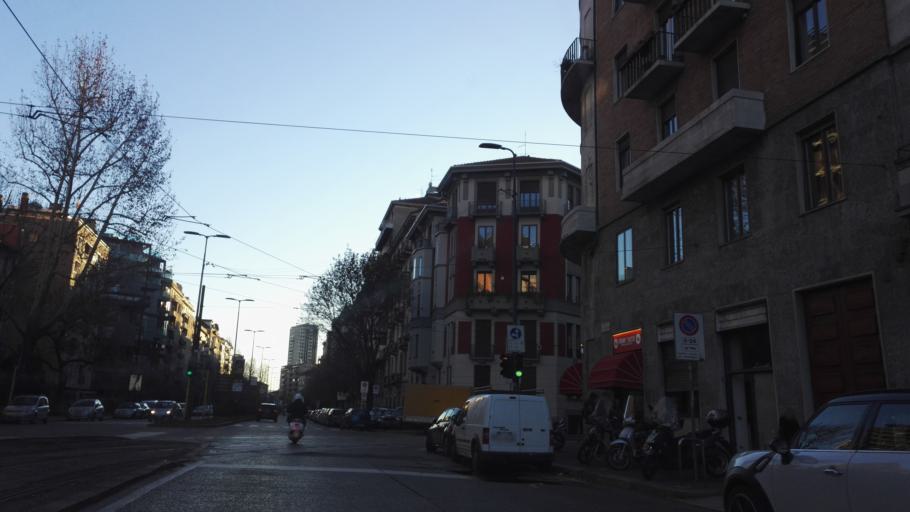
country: IT
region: Lombardy
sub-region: Citta metropolitana di Milano
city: Milano
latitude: 45.4577
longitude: 9.2047
